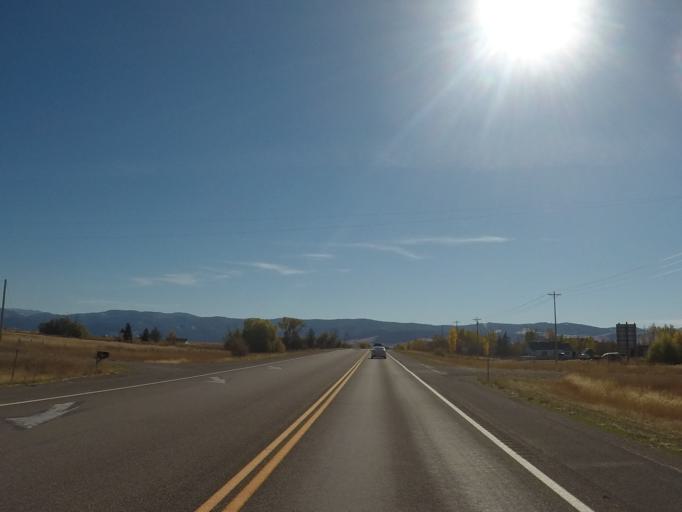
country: US
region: Montana
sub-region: Lake County
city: Ronan
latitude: 47.3489
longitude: -114.0969
